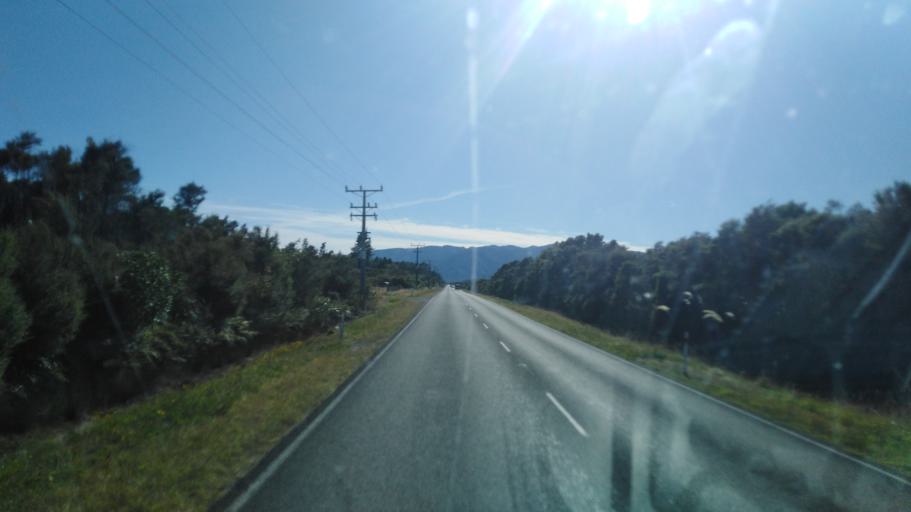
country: NZ
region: West Coast
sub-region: Buller District
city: Westport
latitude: -41.7463
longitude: 171.6830
